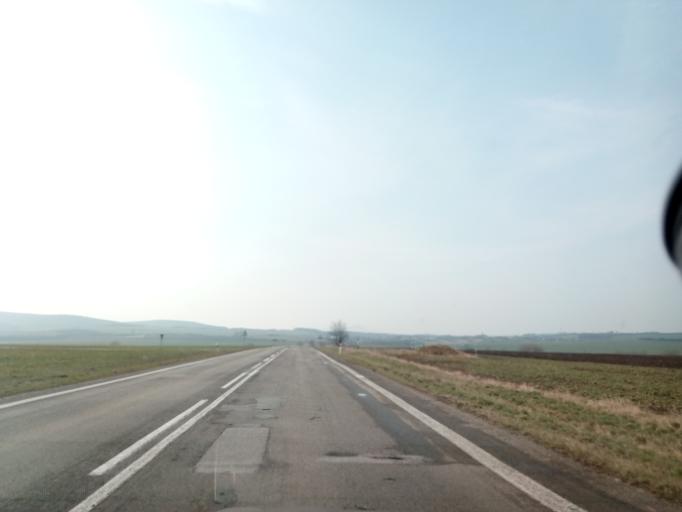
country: SK
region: Kosicky
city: Trebisov
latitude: 48.5436
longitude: 21.6874
